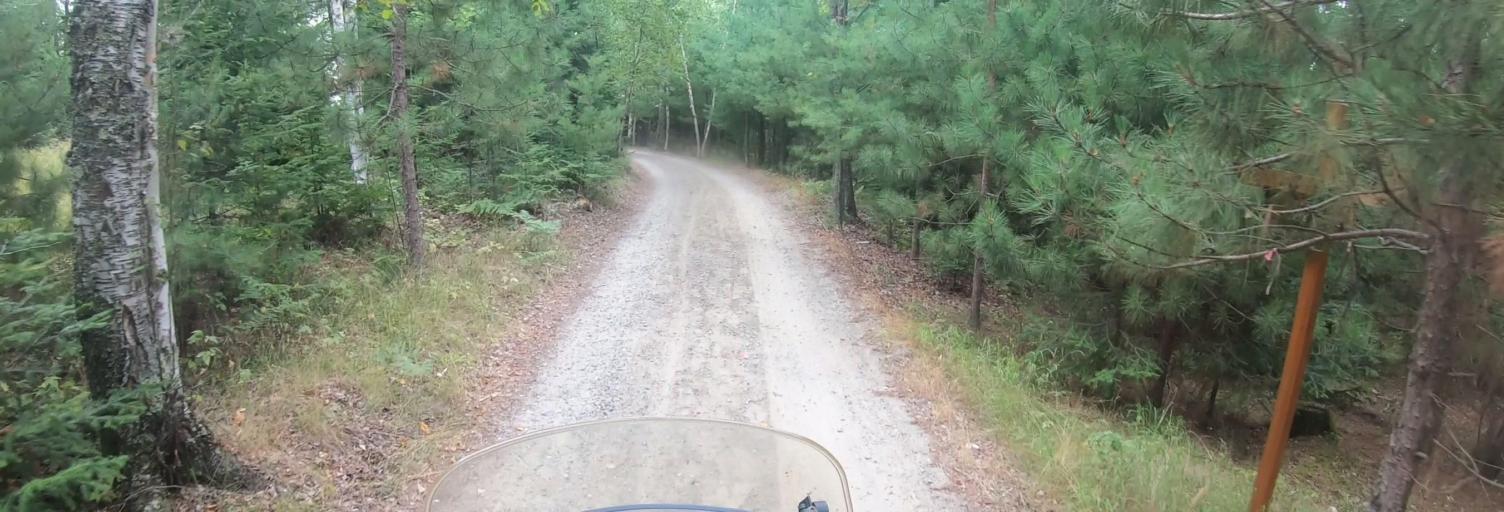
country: US
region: Minnesota
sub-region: Saint Louis County
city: Mountain Iron
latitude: 47.9451
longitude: -92.6304
